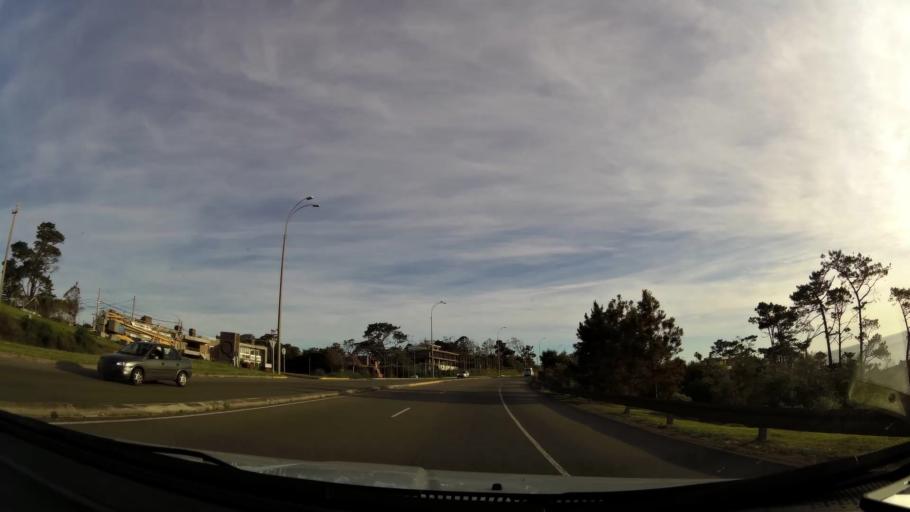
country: UY
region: Maldonado
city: Maldonado
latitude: -34.8920
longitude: -55.0380
